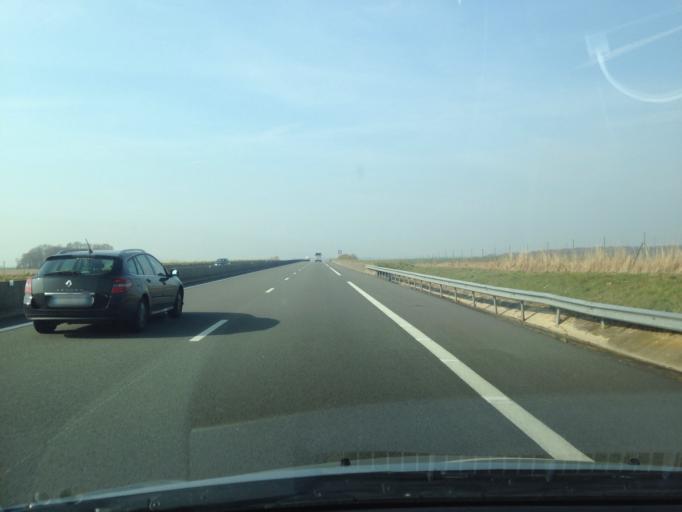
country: FR
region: Picardie
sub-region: Departement de la Somme
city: Rue
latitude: 50.3112
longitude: 1.7232
